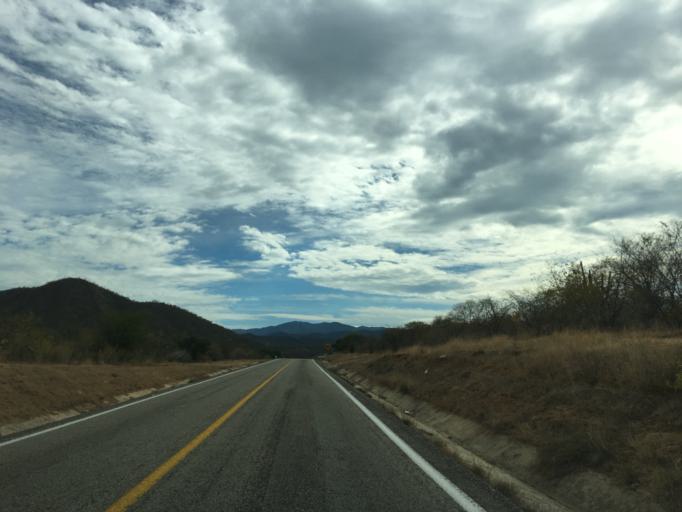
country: MX
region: Baja California Sur
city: Todos Santos
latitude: 23.7776
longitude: -110.0193
